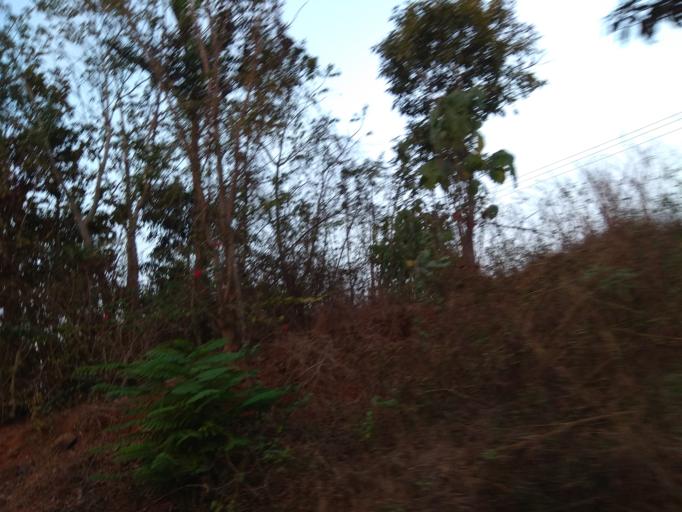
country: IN
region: Karnataka
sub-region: Dakshina Kannada
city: Mangalore
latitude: 12.9350
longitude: 74.8666
